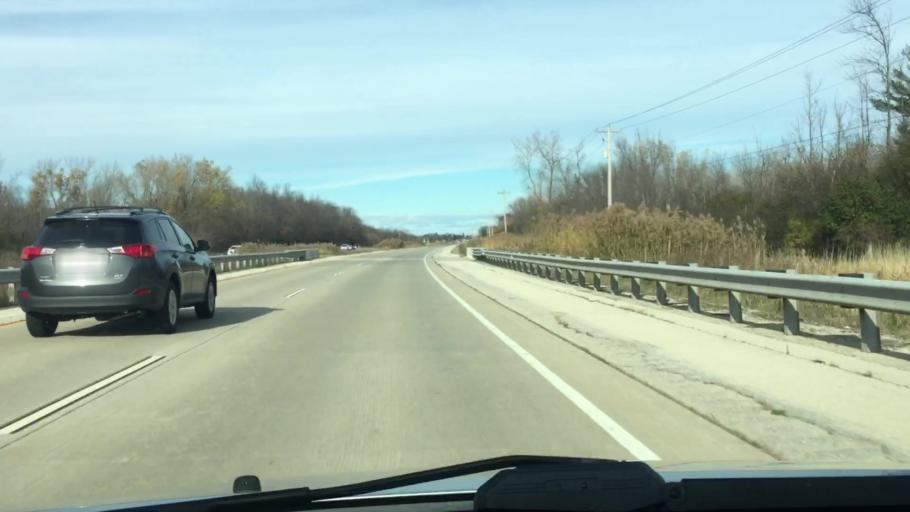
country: US
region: Wisconsin
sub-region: Brown County
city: Bellevue
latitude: 44.5601
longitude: -87.8808
